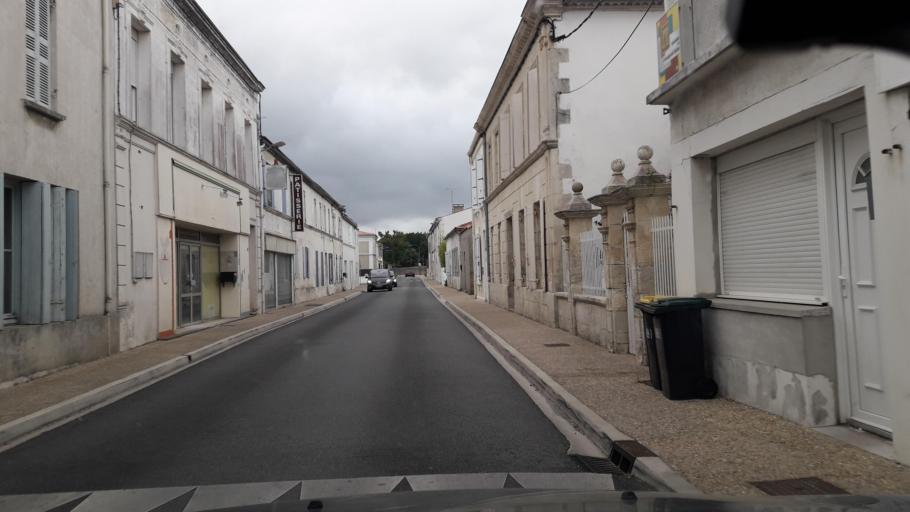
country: FR
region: Poitou-Charentes
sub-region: Departement de la Charente-Maritime
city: Etaules
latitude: 45.7337
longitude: -1.1011
